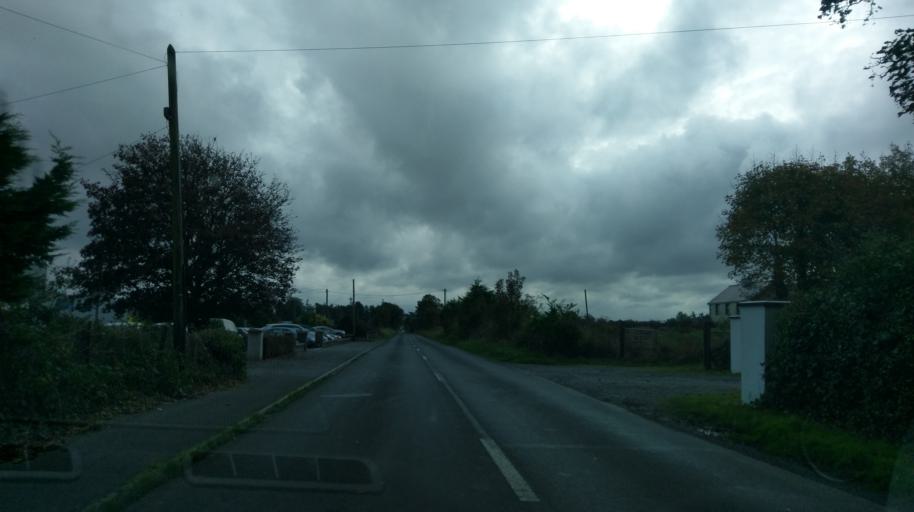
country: IE
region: Connaught
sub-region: County Galway
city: Loughrea
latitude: 53.4587
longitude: -8.4822
